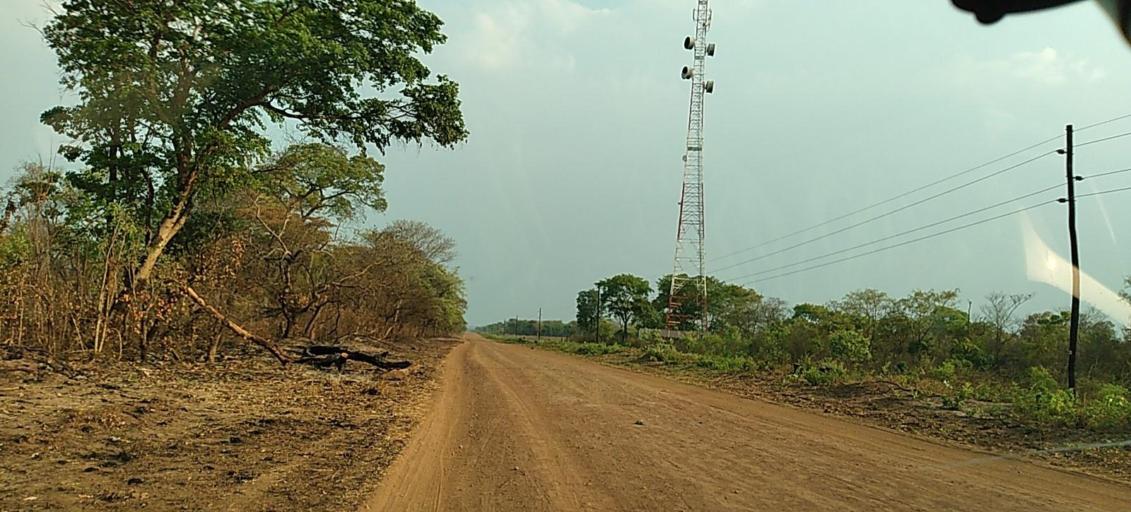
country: ZM
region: Western
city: Lukulu
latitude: -13.9969
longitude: 23.6160
